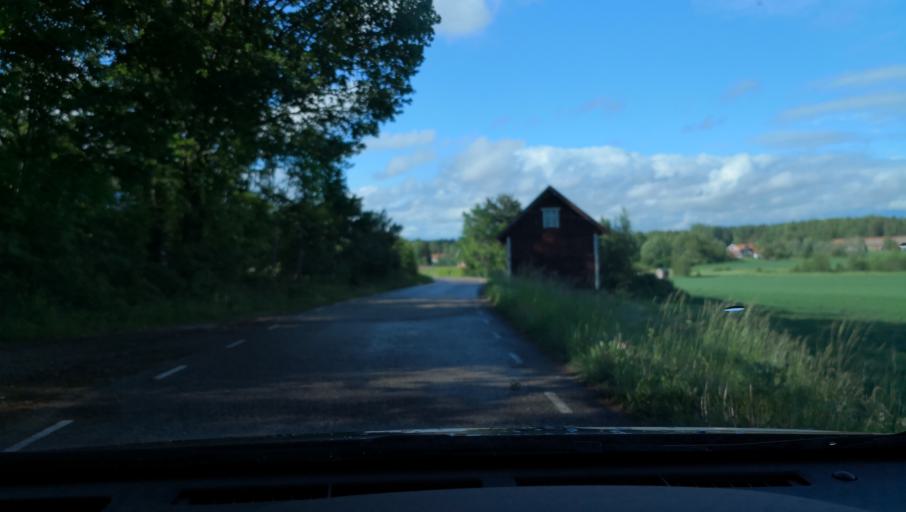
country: SE
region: OErebro
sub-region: Lindesbergs Kommun
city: Fellingsbro
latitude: 59.3217
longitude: 15.6777
